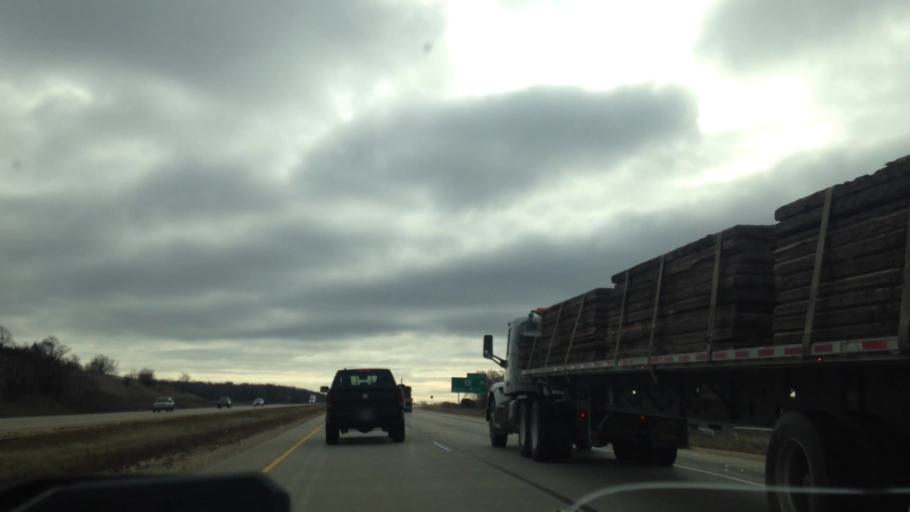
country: US
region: Wisconsin
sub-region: Washington County
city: Slinger
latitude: 43.3756
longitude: -88.3018
